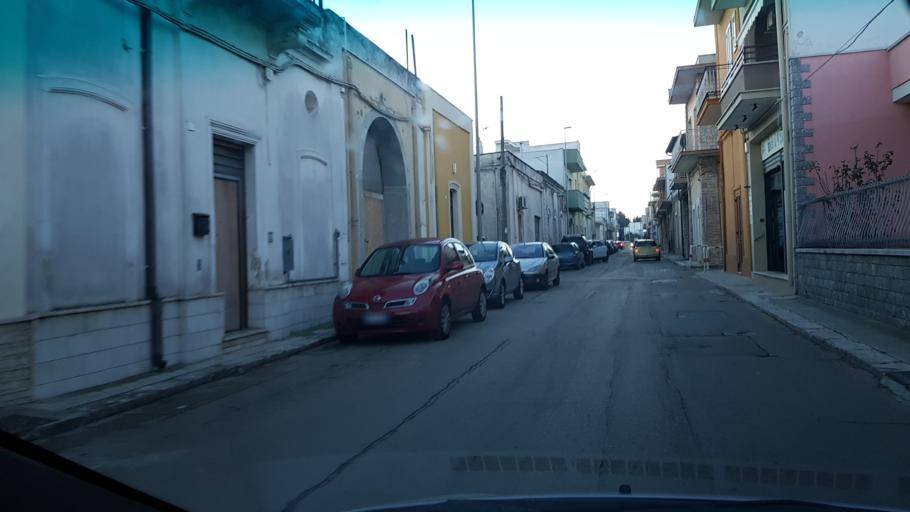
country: IT
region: Apulia
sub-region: Provincia di Brindisi
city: San Pietro Vernotico
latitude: 40.4888
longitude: 17.9929
